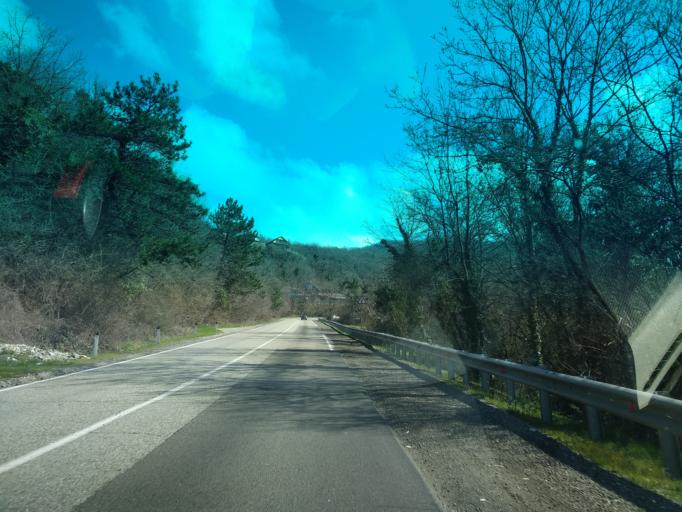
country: RU
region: Krasnodarskiy
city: Tuapse
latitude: 44.0898
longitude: 39.1200
